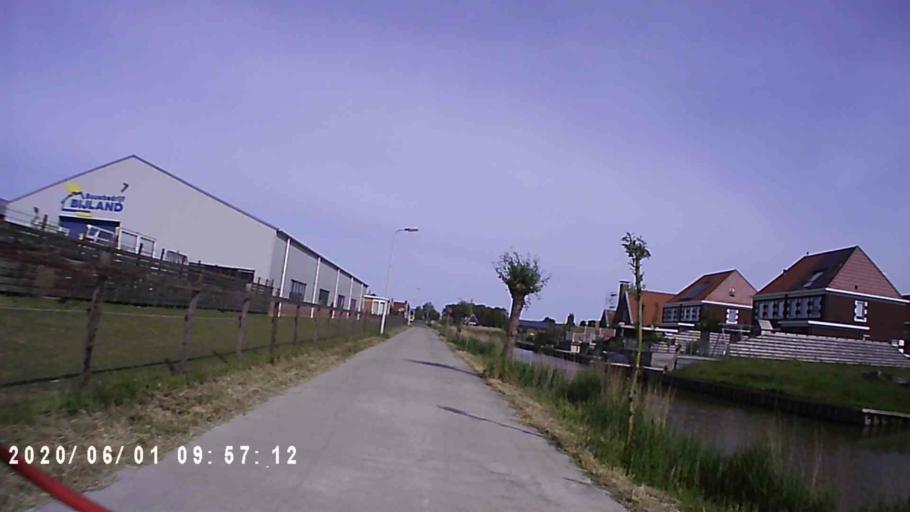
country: NL
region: Friesland
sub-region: Menameradiel
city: Berltsum
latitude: 53.2382
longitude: 5.6464
